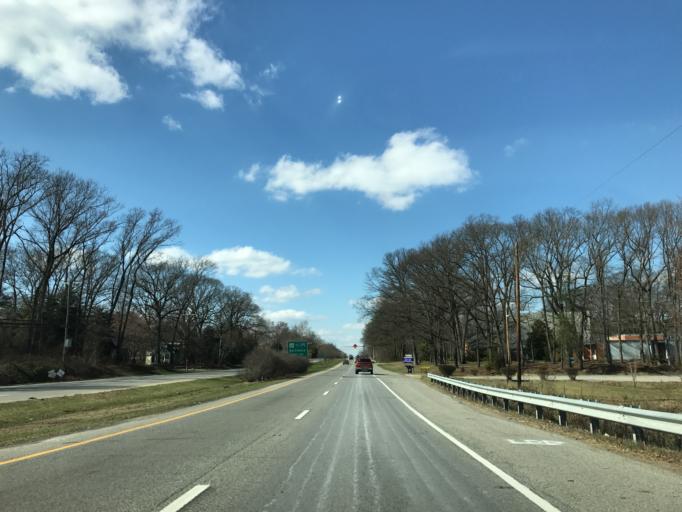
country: US
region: Maryland
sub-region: Anne Arundel County
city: Pasadena
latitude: 39.1042
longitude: -76.5696
